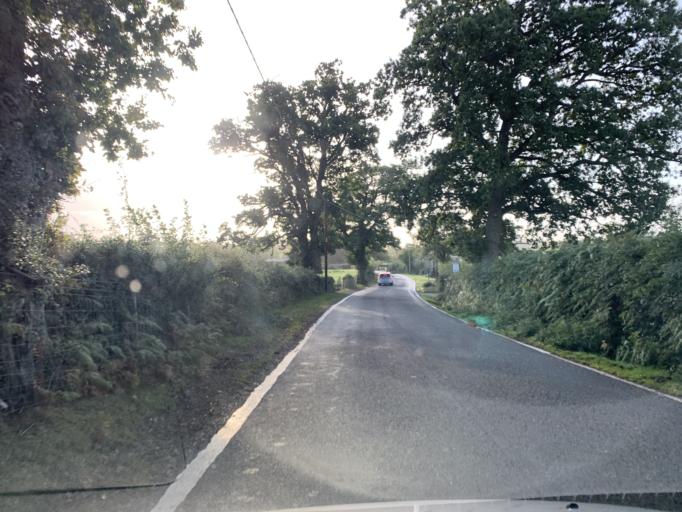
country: GB
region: England
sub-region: Hampshire
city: West Wellow
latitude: 50.9482
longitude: -1.6233
